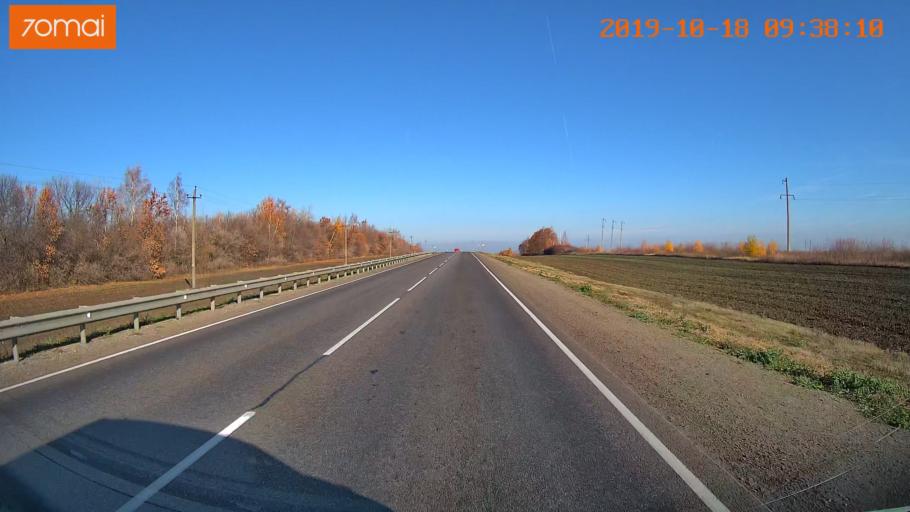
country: RU
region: Tula
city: Yefremov
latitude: 53.2338
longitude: 38.1381
